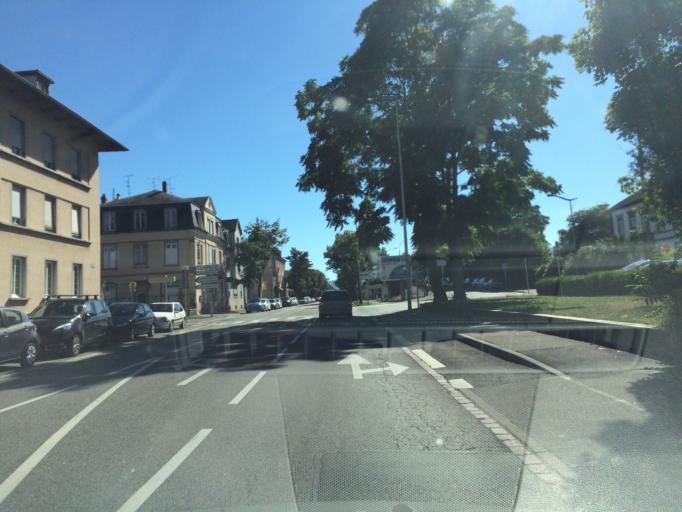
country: FR
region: Alsace
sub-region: Departement du Haut-Rhin
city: Colmar
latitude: 48.0706
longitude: 7.3465
